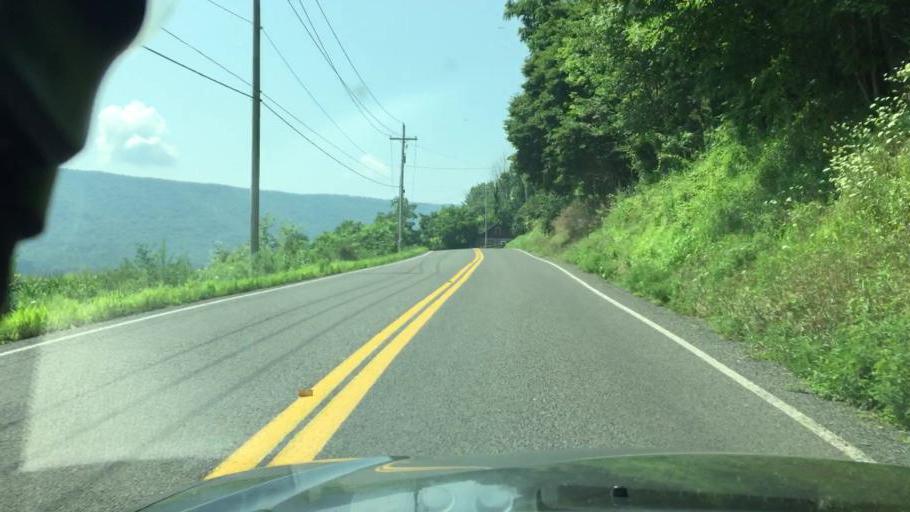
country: US
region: Pennsylvania
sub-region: Columbia County
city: Mifflinville
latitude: 41.0113
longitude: -76.3183
